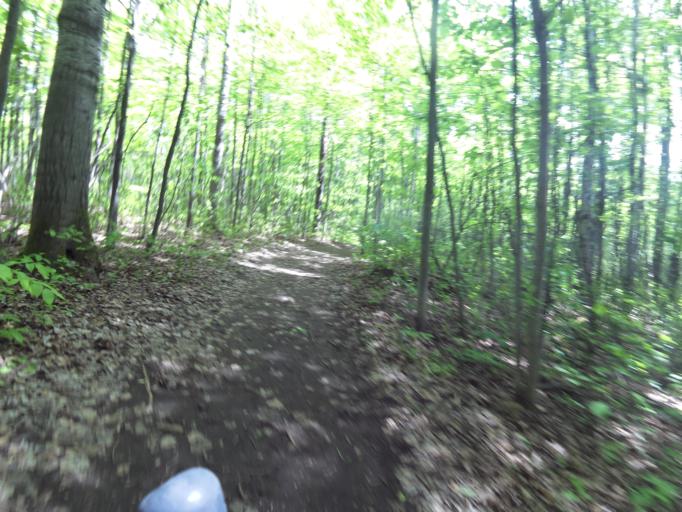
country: CA
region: Ontario
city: Ottawa
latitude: 45.3912
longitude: -75.5289
